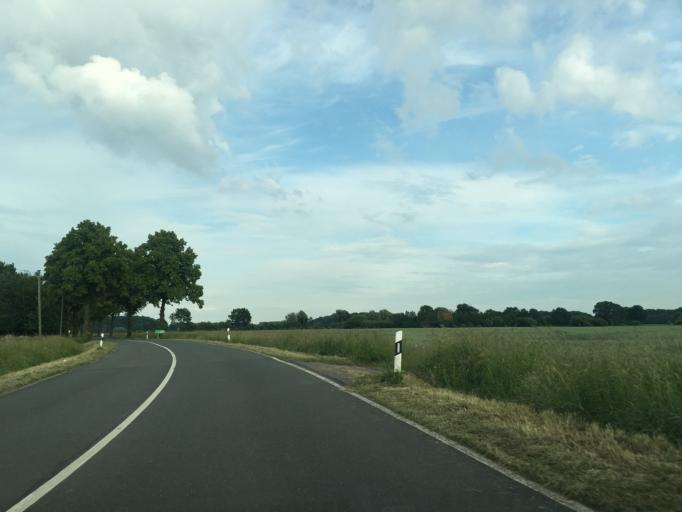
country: DE
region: North Rhine-Westphalia
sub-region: Regierungsbezirk Munster
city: Altenberge
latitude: 51.9930
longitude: 7.4788
